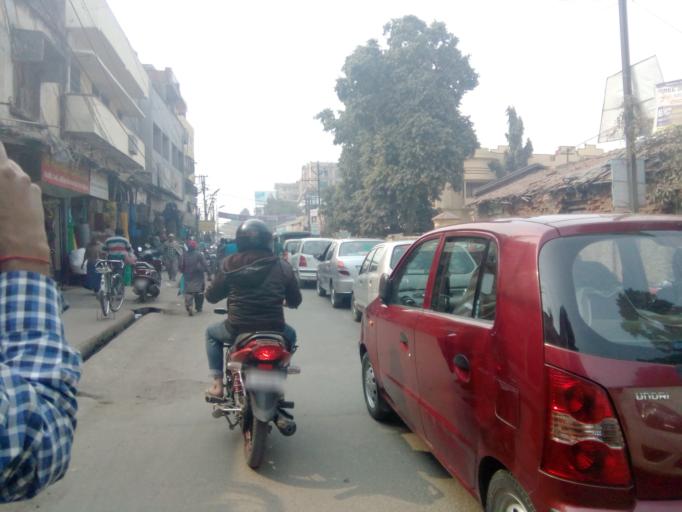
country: IN
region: Bihar
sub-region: Patna
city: Patna
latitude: 25.6194
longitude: 85.1545
